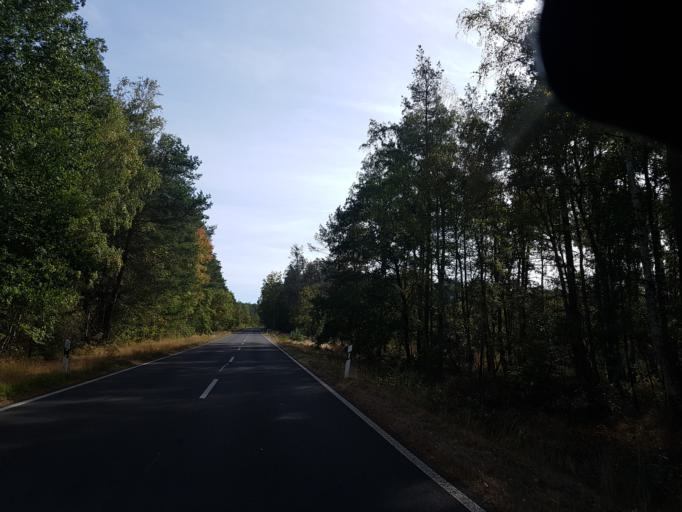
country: DE
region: Brandenburg
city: Schlieben
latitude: 51.6836
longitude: 13.4558
